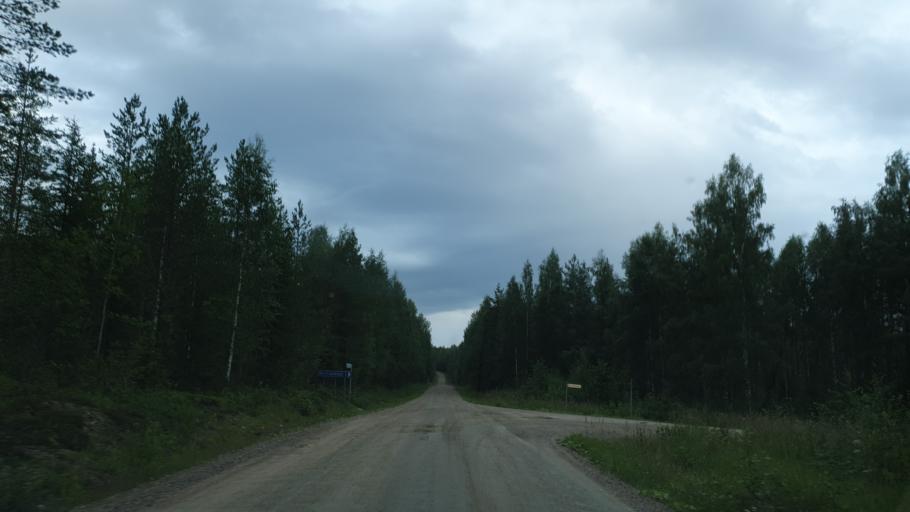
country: FI
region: Kainuu
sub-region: Kehys-Kainuu
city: Kuhmo
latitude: 64.1933
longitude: 29.3720
